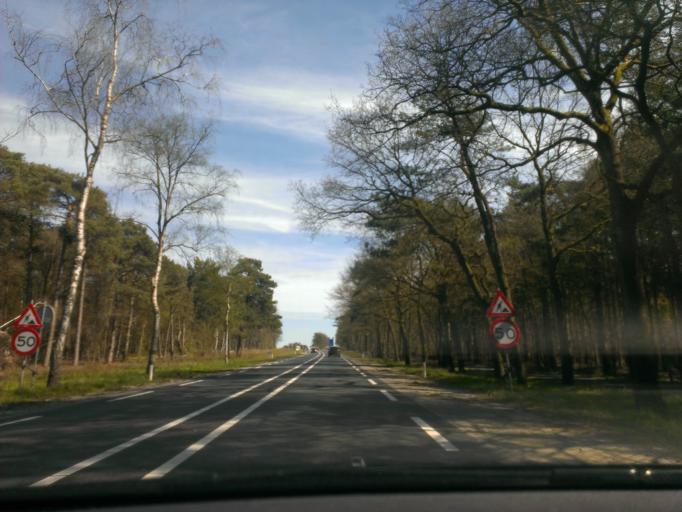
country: NL
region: Overijssel
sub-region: Gemeente Twenterand
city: Den Ham
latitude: 52.3672
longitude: 6.4320
